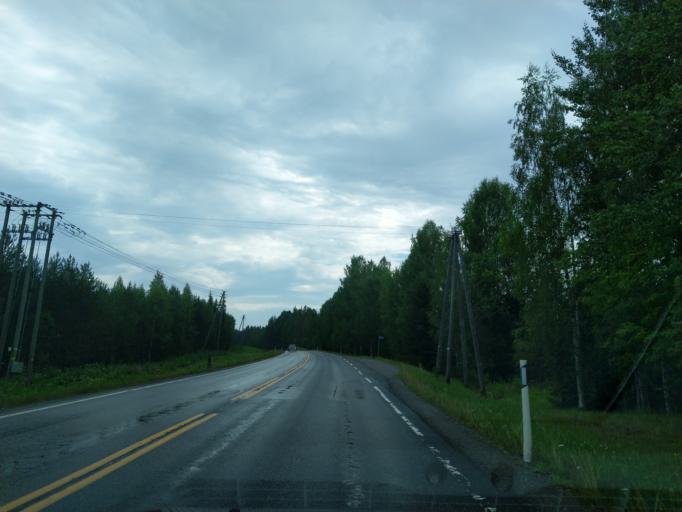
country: FI
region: Southern Savonia
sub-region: Savonlinna
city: Punkaharju
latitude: 61.6702
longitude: 29.4123
